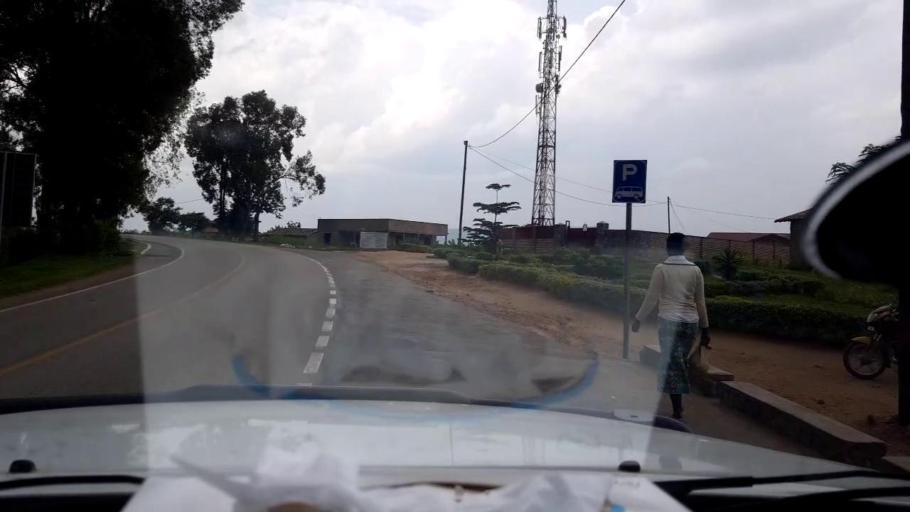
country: RW
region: Southern Province
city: Gitarama
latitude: -2.1528
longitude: 29.7483
